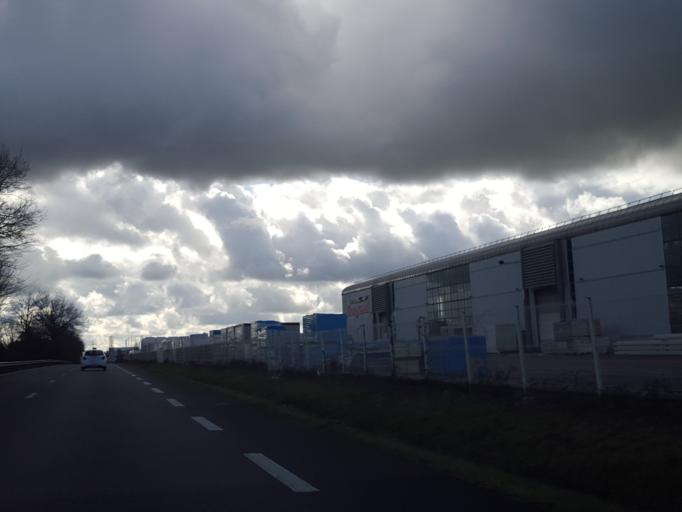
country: FR
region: Pays de la Loire
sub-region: Departement de la Vendee
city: Mouilleron-le-Captif
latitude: 46.7227
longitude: -1.4301
